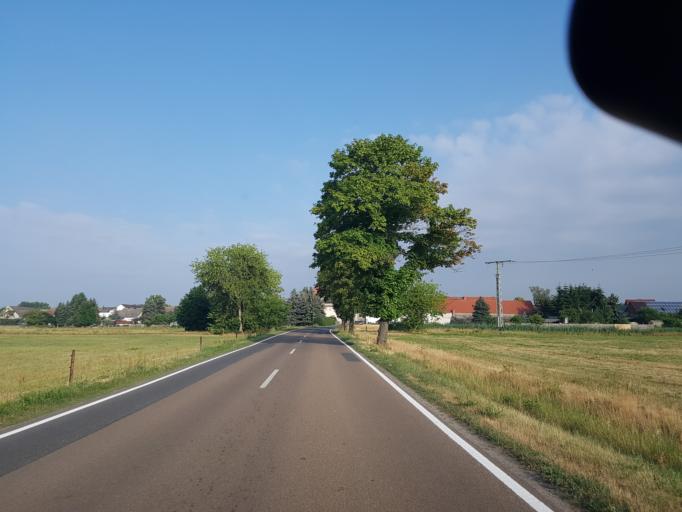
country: DE
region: Saxony-Anhalt
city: Holzdorf
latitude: 51.8537
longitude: 13.1060
